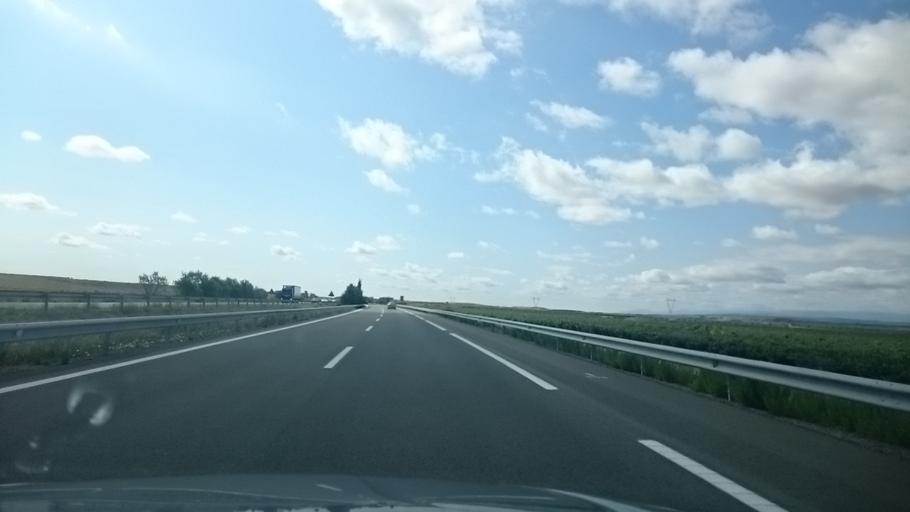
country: ES
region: La Rioja
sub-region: Provincia de La Rioja
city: Rincon de Soto
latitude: 42.1694
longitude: -1.8312
